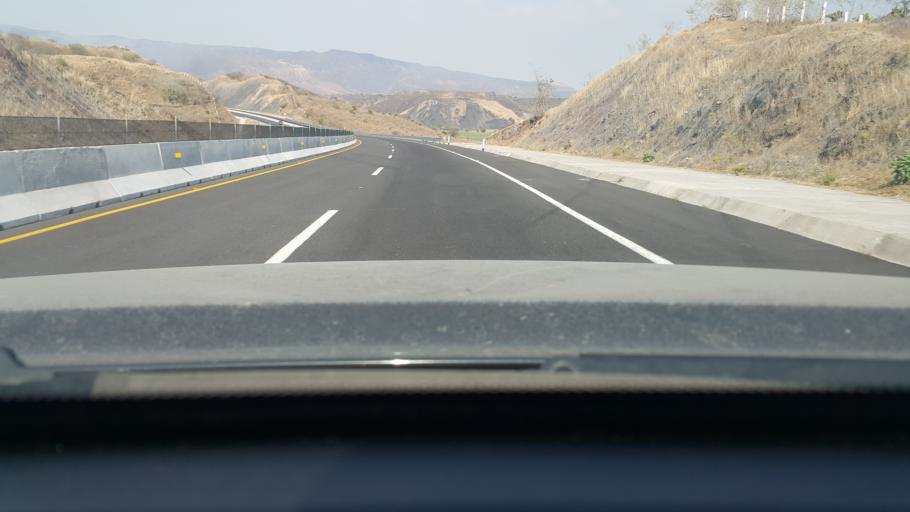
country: MX
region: Nayarit
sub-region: Ahuacatlan
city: Ahuacatlan
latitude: 21.0673
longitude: -104.4653
